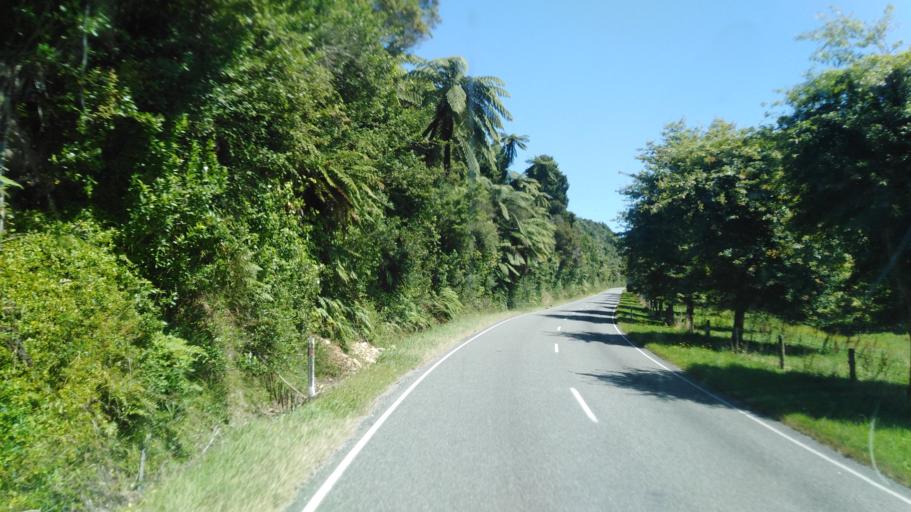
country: NZ
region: West Coast
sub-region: Buller District
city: Westport
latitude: -41.2602
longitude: 172.1223
